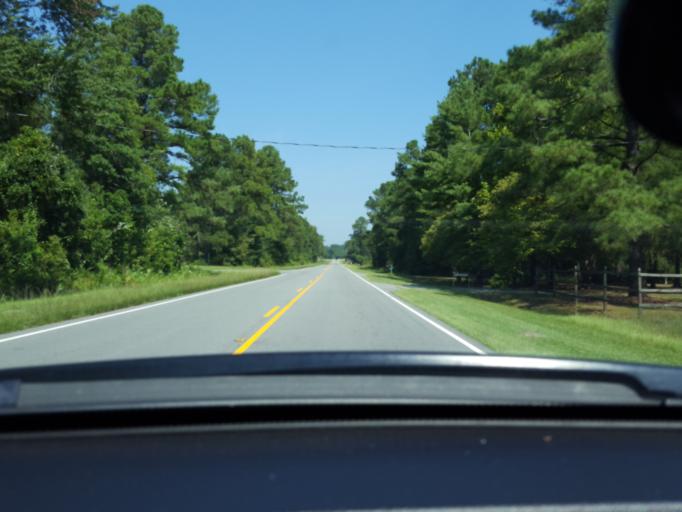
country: US
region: North Carolina
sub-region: Bladen County
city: Elizabethtown
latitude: 34.6717
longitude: -78.4901
